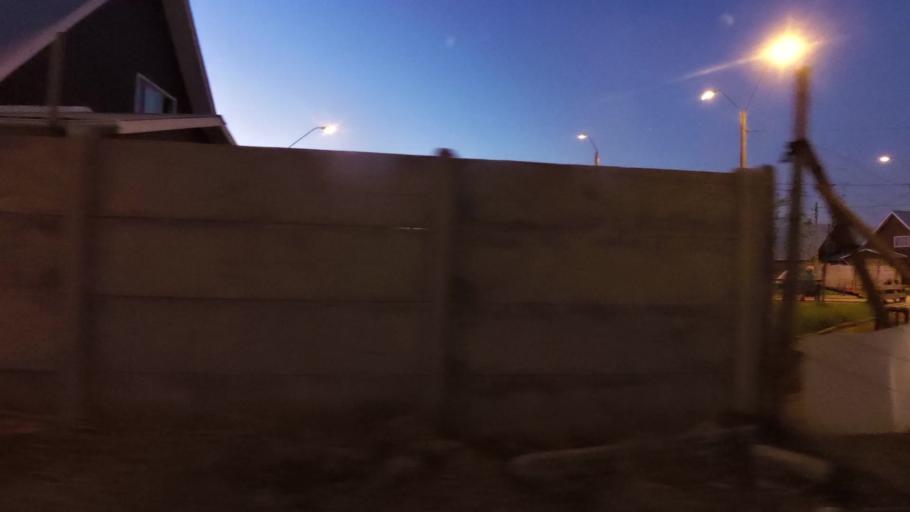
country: CL
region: Maule
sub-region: Provincia de Talca
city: Talca
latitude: -35.4427
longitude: -71.6216
